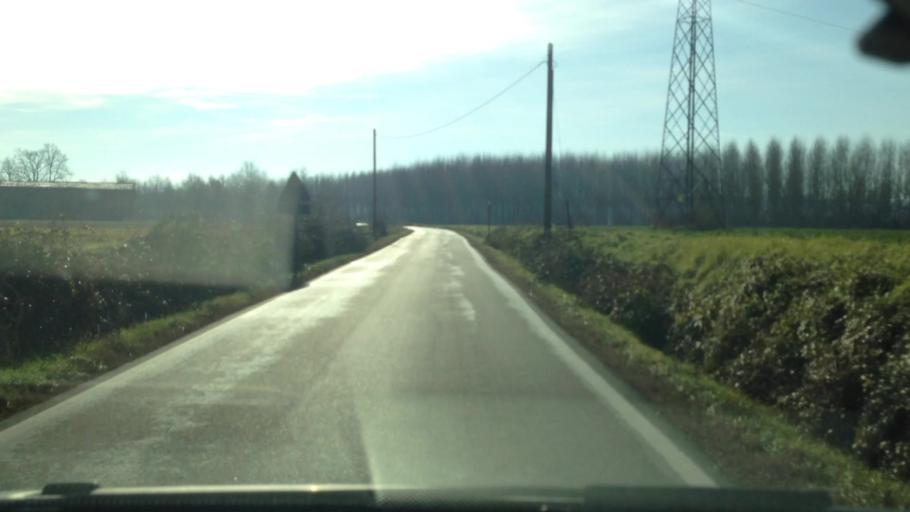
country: IT
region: Piedmont
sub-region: Provincia di Alessandria
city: Quattordio
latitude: 44.8890
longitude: 8.4049
